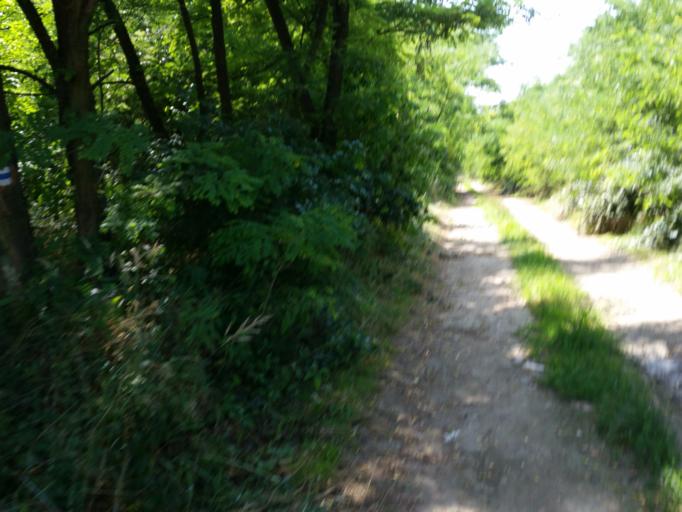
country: HU
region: Vas
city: Sarvar
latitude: 47.2105
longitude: 17.0130
